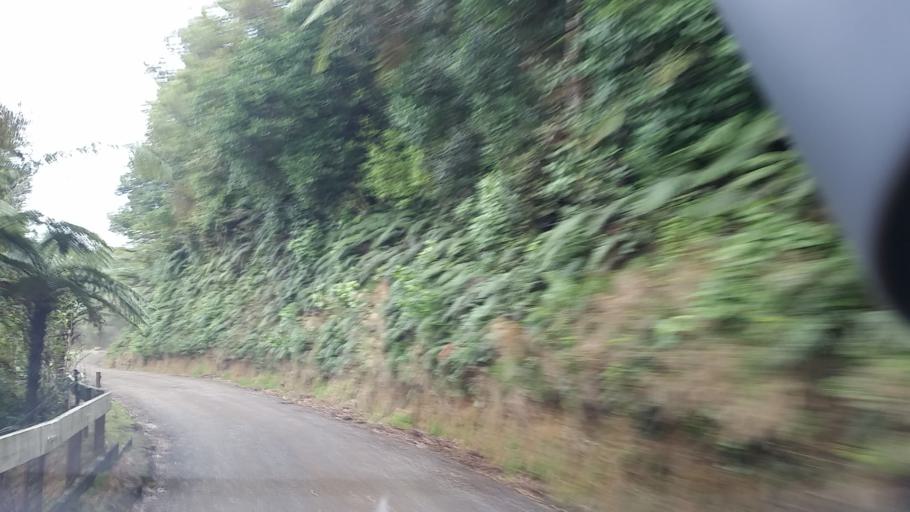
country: NZ
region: Taranaki
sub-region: New Plymouth District
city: Waitara
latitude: -39.0413
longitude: 174.4125
